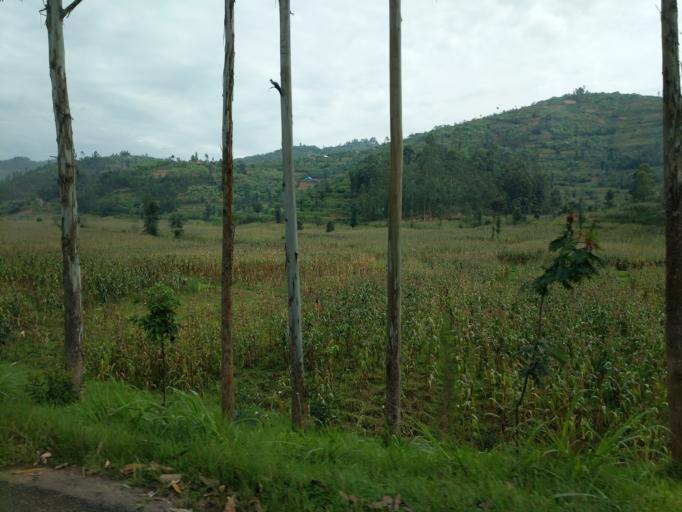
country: RW
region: Northern Province
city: Musanze
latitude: -1.5758
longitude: 29.7209
